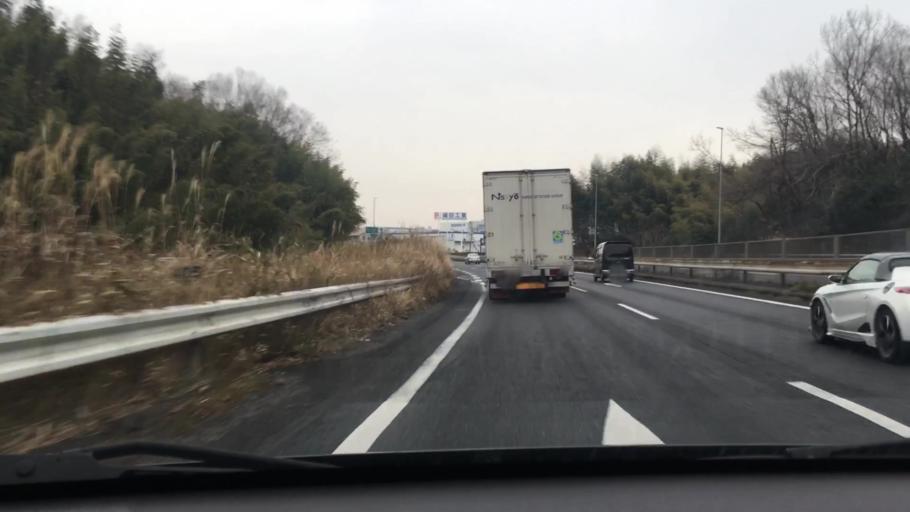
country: JP
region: Mie
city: Ueno-ebisumachi
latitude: 34.7045
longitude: 136.0733
